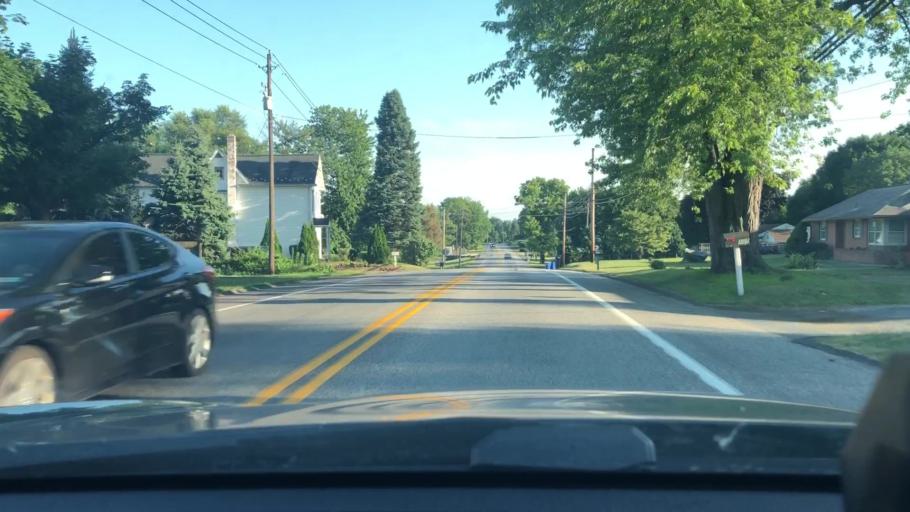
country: US
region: Pennsylvania
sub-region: Cumberland County
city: Mechanicsburg
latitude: 40.2289
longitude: -77.0072
